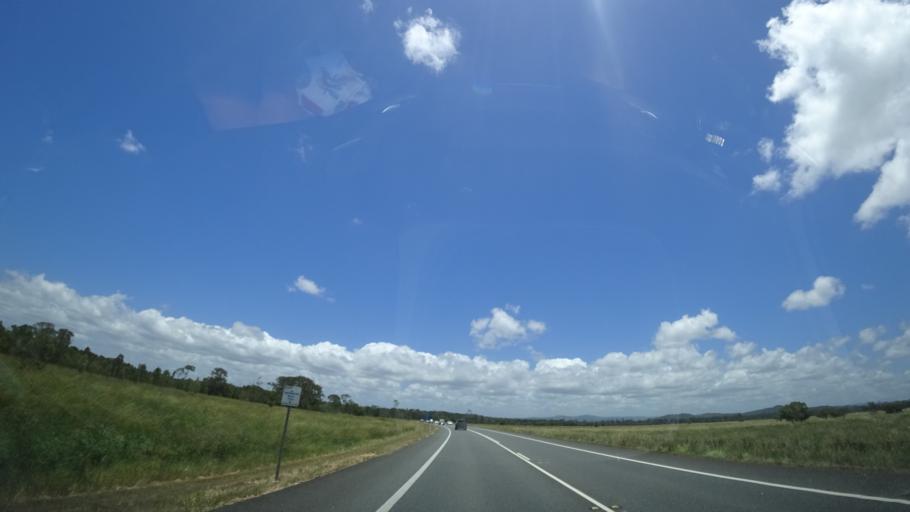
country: AU
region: Queensland
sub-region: Sunshine Coast
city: Little Mountain
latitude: -26.7686
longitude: 153.0857
